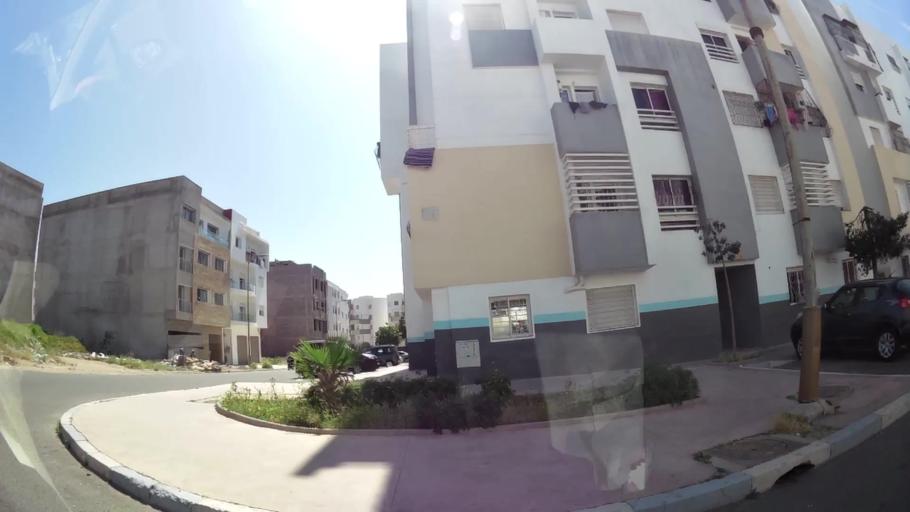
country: MA
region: Oued ed Dahab-Lagouira
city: Dakhla
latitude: 30.4362
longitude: -9.5576
